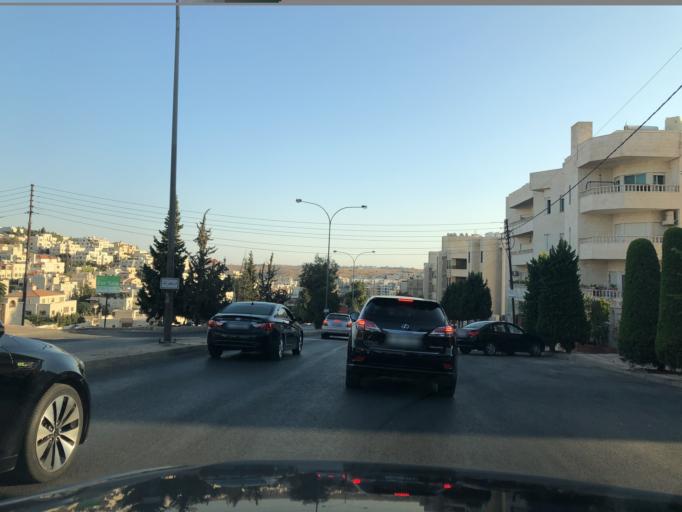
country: JO
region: Amman
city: Wadi as Sir
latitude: 31.9449
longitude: 35.8700
